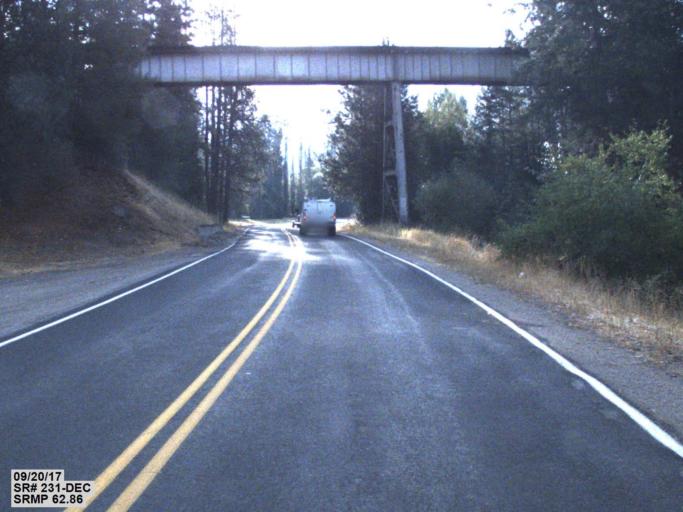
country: US
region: Washington
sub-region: Stevens County
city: Chewelah
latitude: 48.0581
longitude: -117.7533
